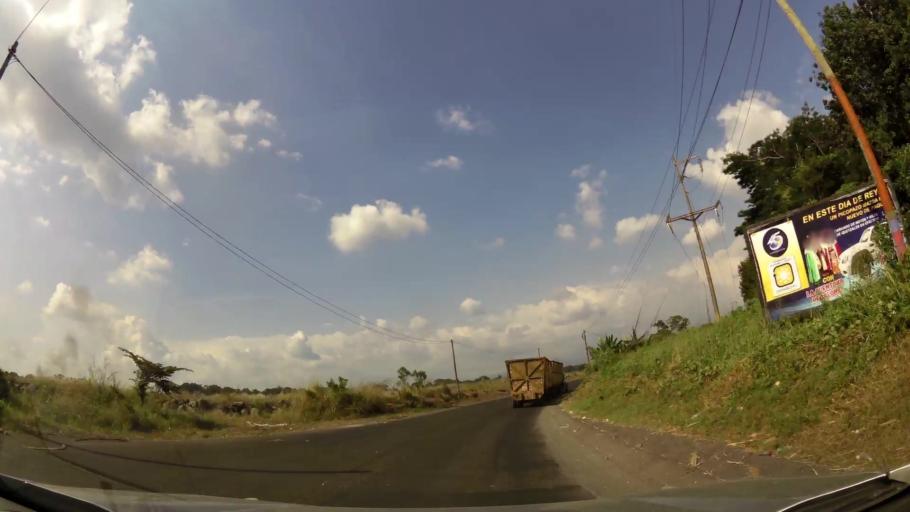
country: GT
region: Retalhuleu
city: San Sebastian
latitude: 14.5537
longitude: -91.6399
